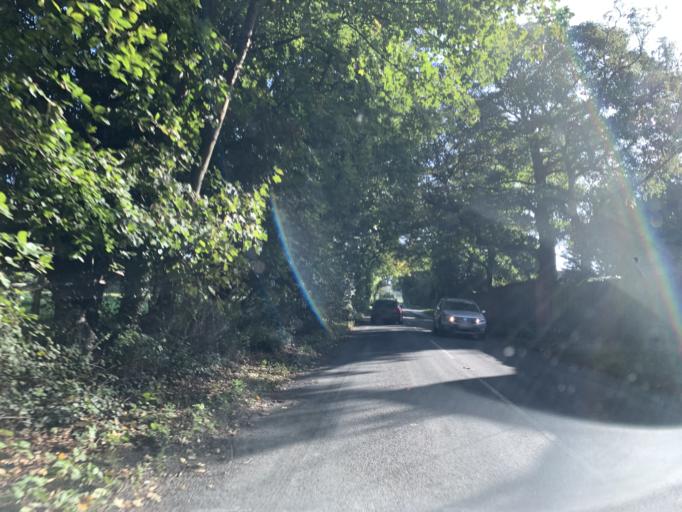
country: GB
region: England
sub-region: Wiltshire
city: Downton
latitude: 50.9926
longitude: -1.7314
